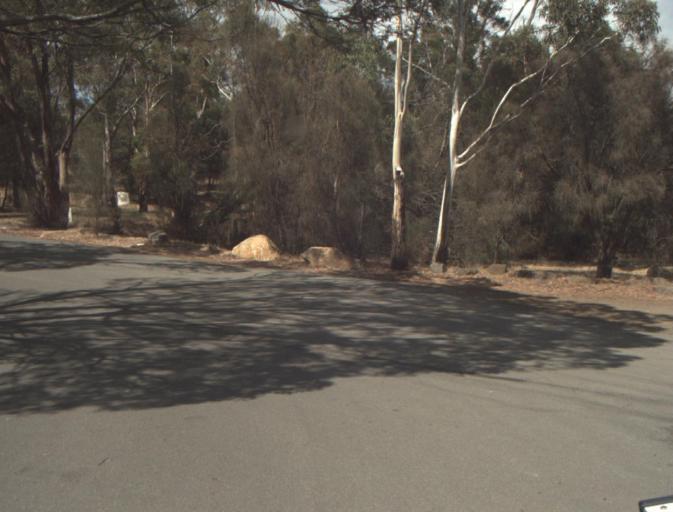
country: AU
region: Tasmania
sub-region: Launceston
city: West Launceston
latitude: -41.4494
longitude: 147.1200
